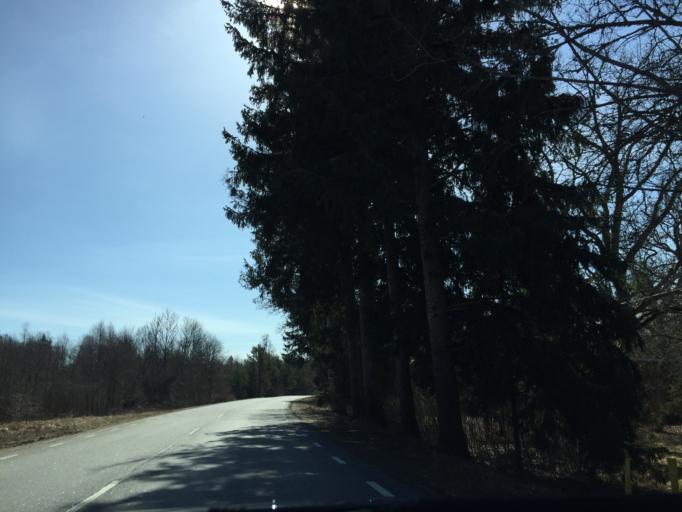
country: EE
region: Laeaene
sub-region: Lihula vald
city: Lihula
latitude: 58.6143
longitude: 23.6929
